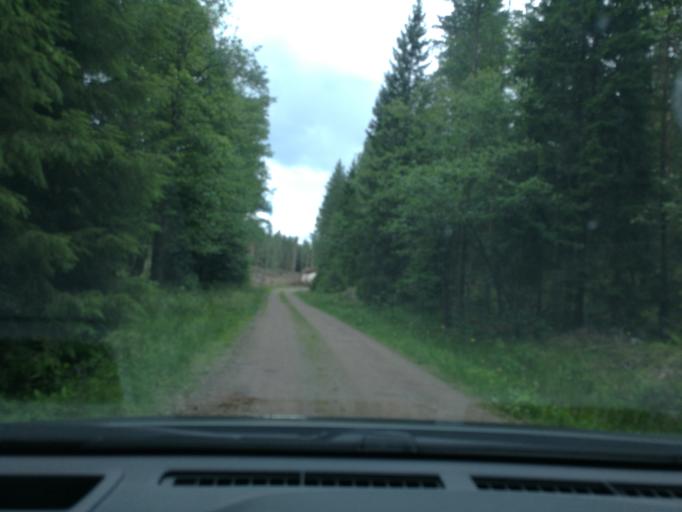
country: SE
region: Vaestmanland
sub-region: Vasteras
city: Skultuna
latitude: 59.8035
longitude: 16.3325
